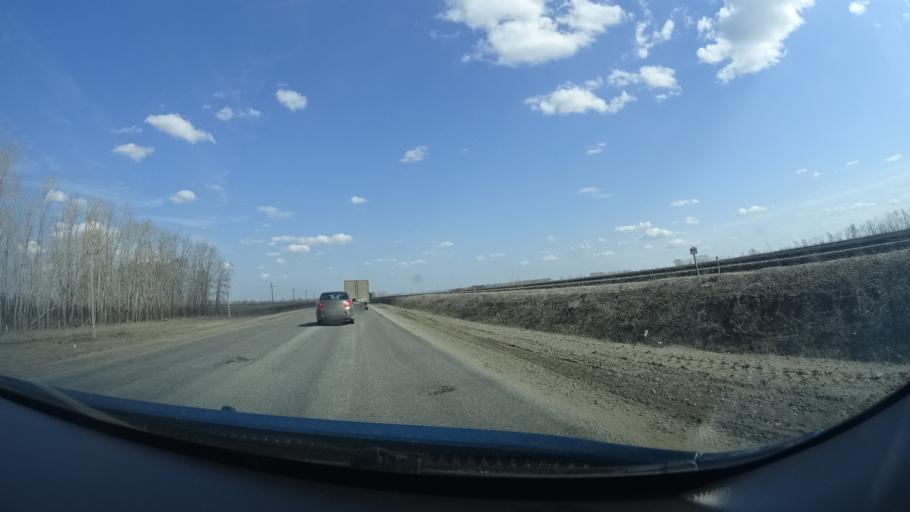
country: RU
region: Bashkortostan
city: Buzdyak
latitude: 54.6400
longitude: 54.4941
